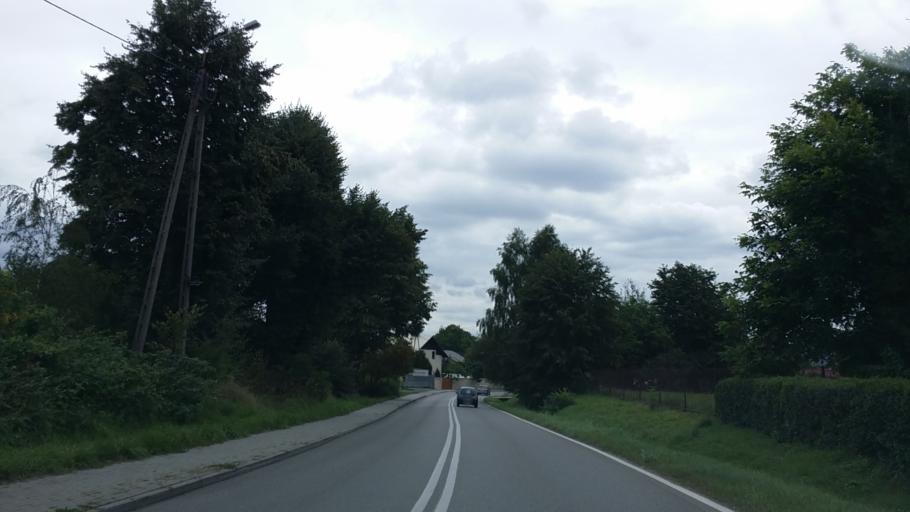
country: PL
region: Lesser Poland Voivodeship
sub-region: Powiat wadowicki
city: Tomice
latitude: 49.8894
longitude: 19.4769
